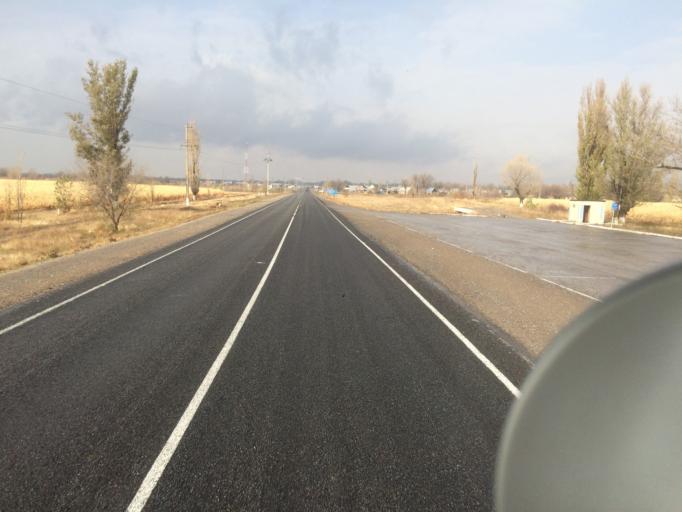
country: KZ
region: Zhambyl
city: Georgiyevka
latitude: 43.1555
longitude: 74.6008
